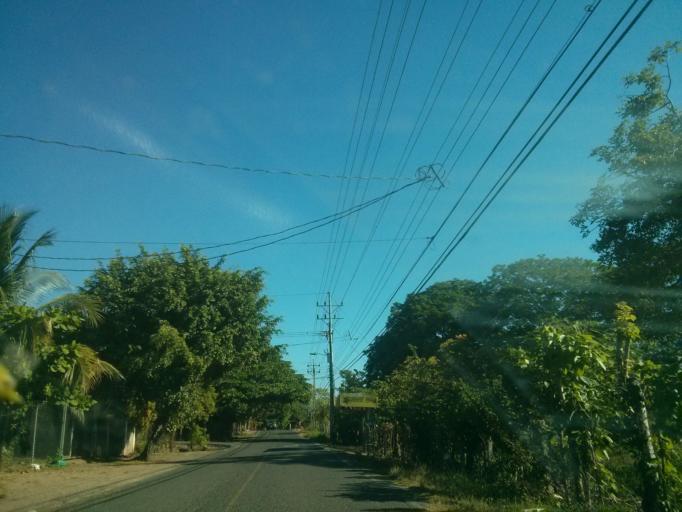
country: CR
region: Puntarenas
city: Paquera
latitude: 9.6906
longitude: -85.1019
